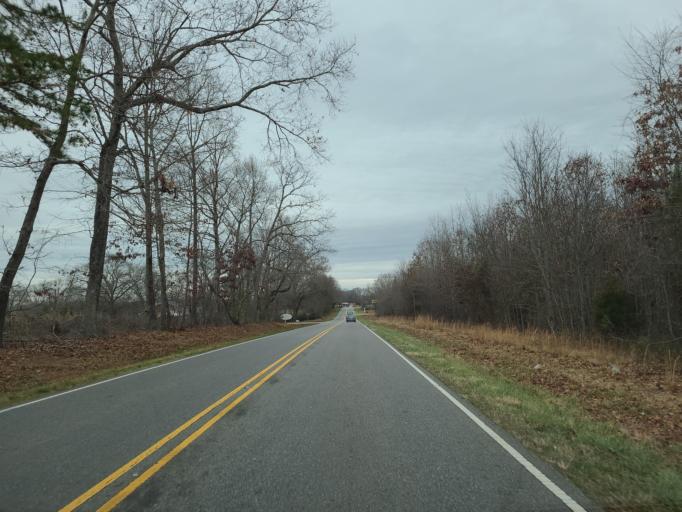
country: US
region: North Carolina
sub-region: Cleveland County
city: Shelby
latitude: 35.3589
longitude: -81.5725
